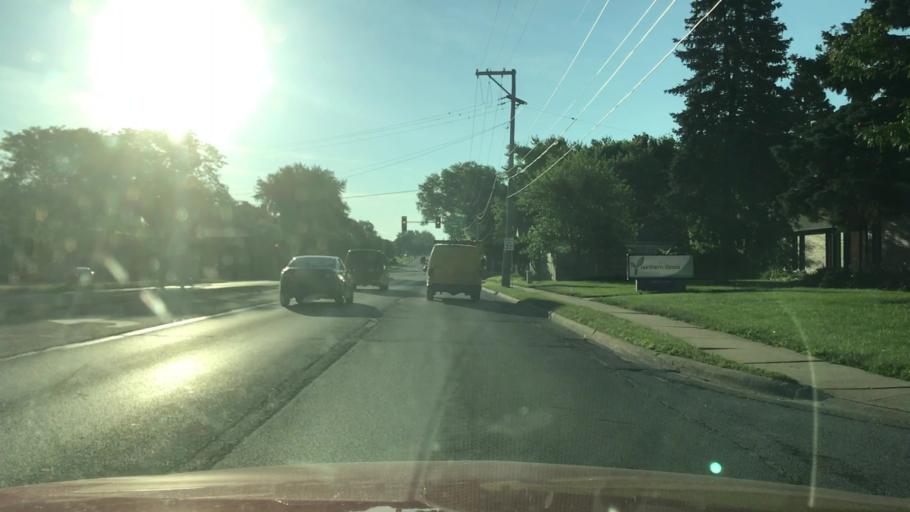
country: US
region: Illinois
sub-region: Winnebago County
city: Rockford
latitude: 42.2527
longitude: -89.0275
